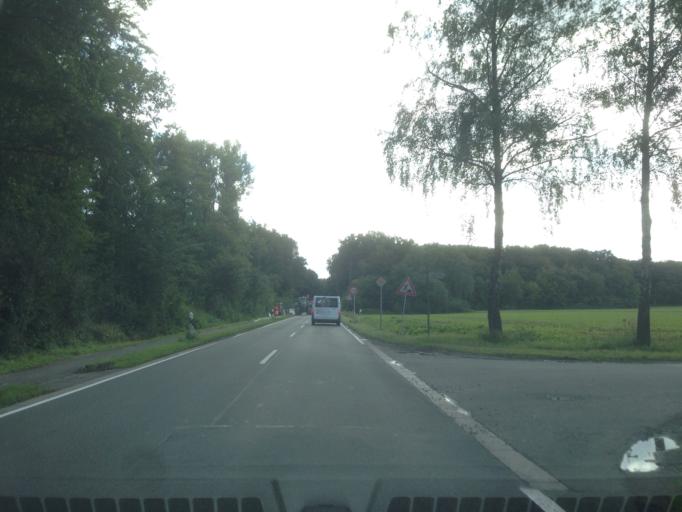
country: DE
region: North Rhine-Westphalia
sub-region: Regierungsbezirk Munster
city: Muenster
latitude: 51.9097
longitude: 7.5705
